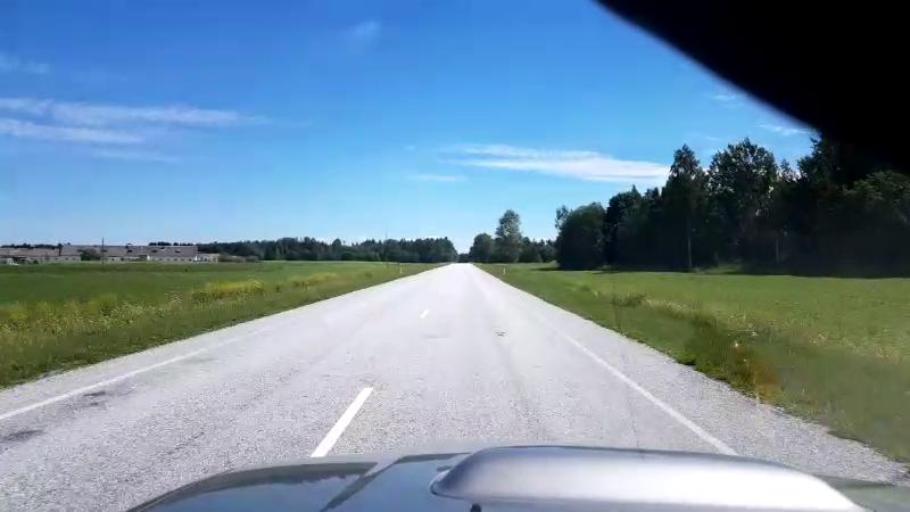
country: EE
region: Laeaene-Virumaa
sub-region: Rakke vald
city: Rakke
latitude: 58.9545
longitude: 26.1732
